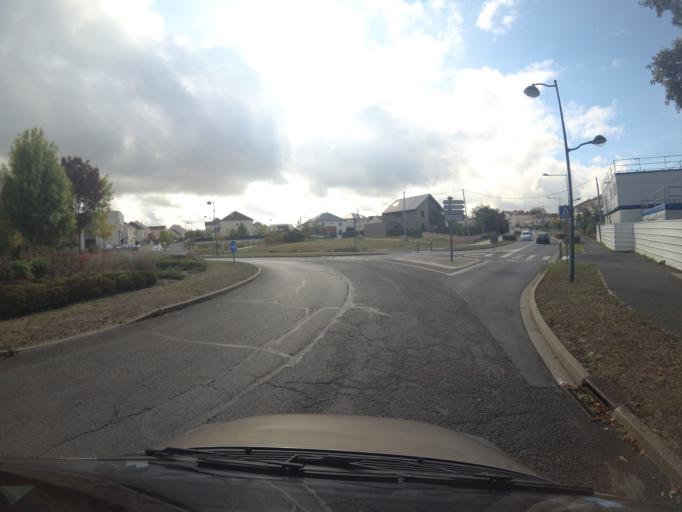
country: FR
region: Ile-de-France
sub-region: Departement de Seine-et-Marne
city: Montevrain
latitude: 48.8673
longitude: 2.7542
